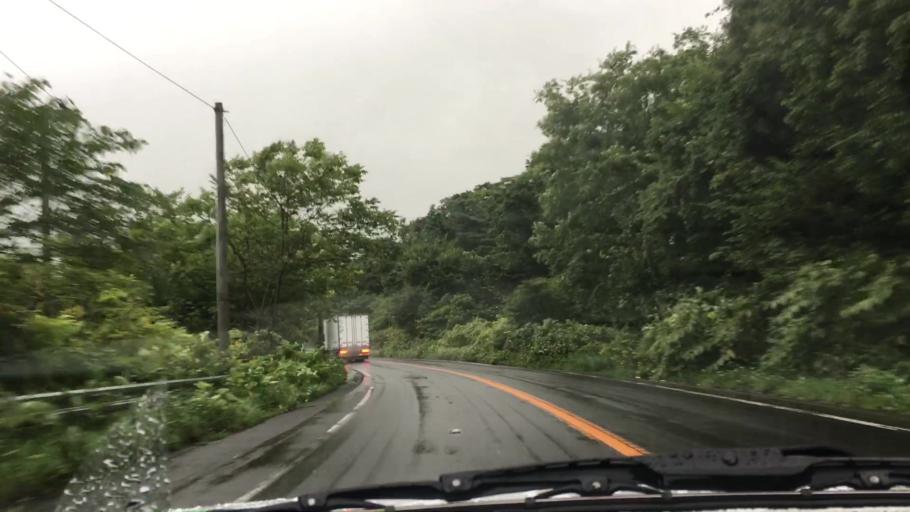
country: JP
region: Hokkaido
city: Niseko Town
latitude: 42.5926
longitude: 140.5958
